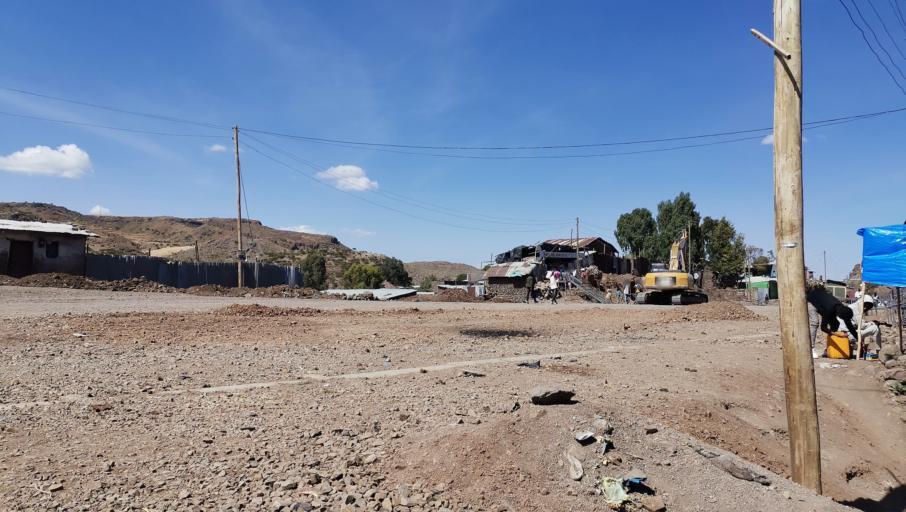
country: ET
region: Tigray
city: Korem
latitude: 12.6277
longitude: 39.0350
